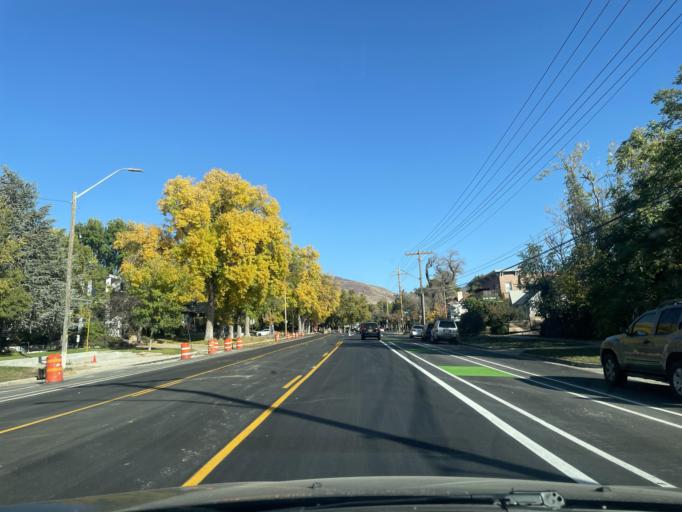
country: US
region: Utah
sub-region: Salt Lake County
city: Salt Lake City
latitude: 40.7650
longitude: -111.8668
